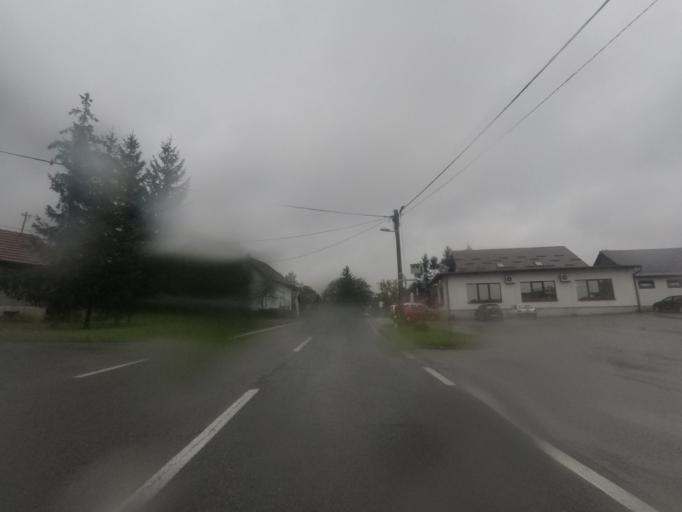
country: HR
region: Karlovacka
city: Ostarije
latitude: 45.1838
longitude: 15.2873
